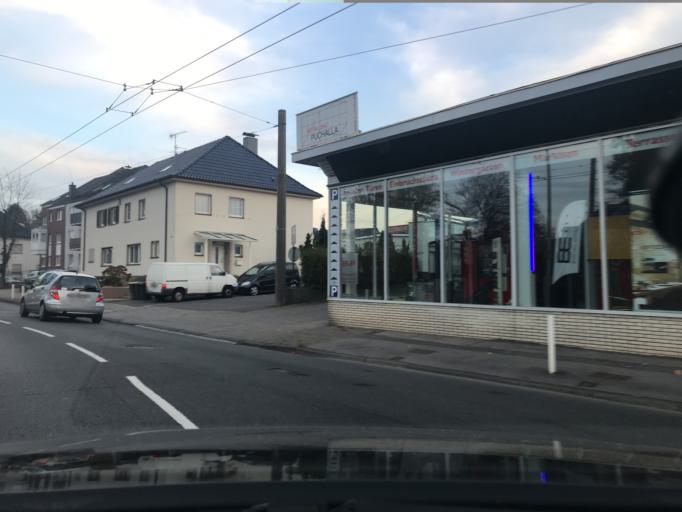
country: DE
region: North Rhine-Westphalia
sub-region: Regierungsbezirk Dusseldorf
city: Solingen
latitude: 51.1719
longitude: 7.0681
